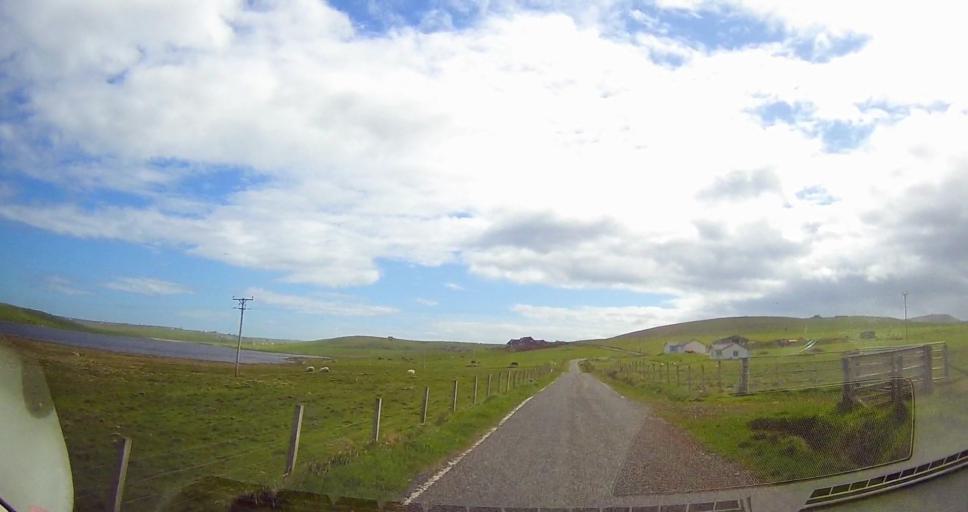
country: GB
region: Scotland
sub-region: Shetland Islands
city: Sandwick
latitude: 59.9357
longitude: -1.3460
